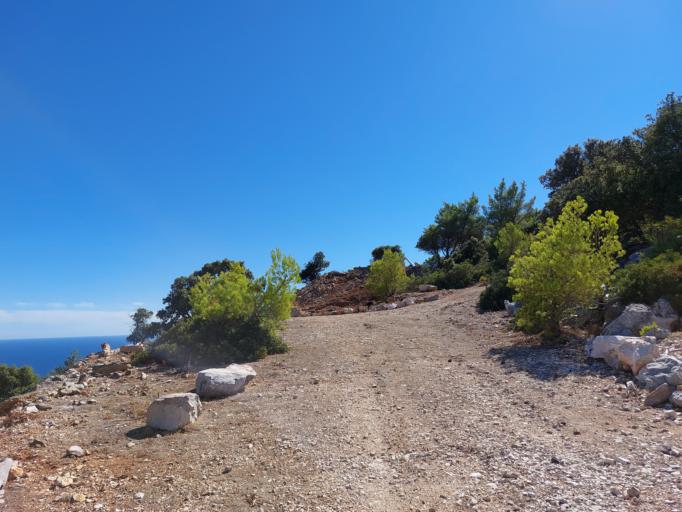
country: HR
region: Dubrovacko-Neretvanska
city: Smokvica
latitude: 42.7401
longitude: 16.8402
